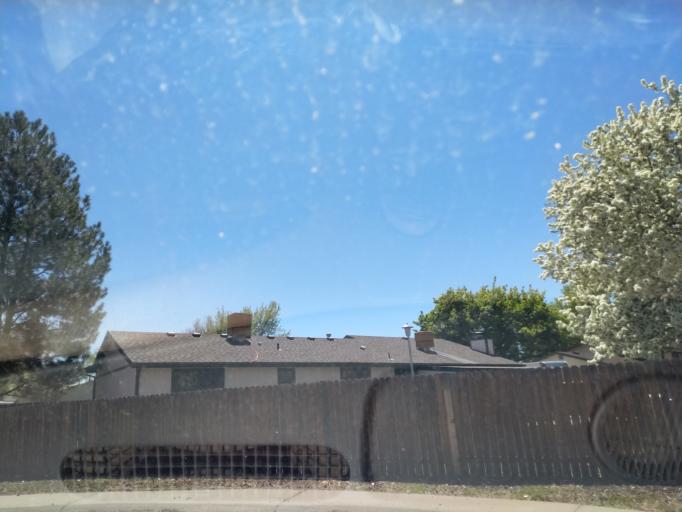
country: US
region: Colorado
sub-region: Mesa County
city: Grand Junction
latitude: 39.0954
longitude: -108.5391
